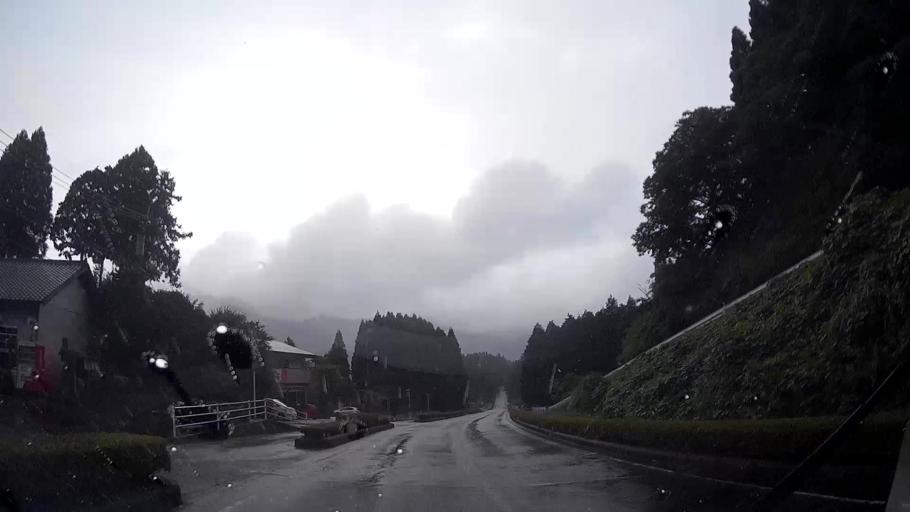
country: JP
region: Kumamoto
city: Aso
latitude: 32.8562
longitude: 131.0117
